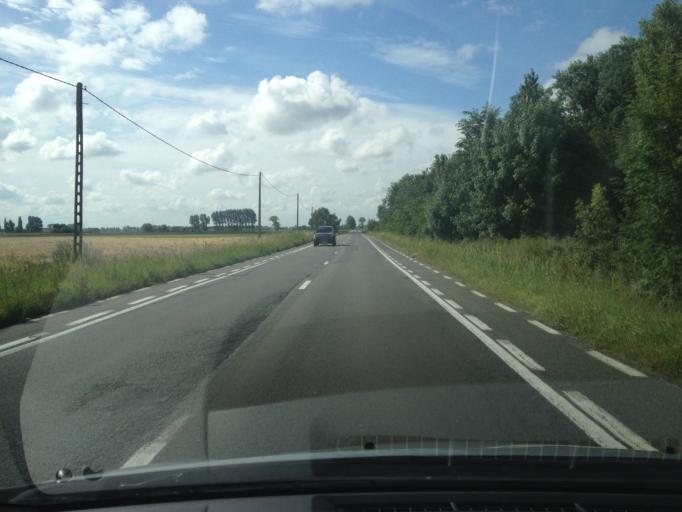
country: BE
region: Flanders
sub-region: Provincie West-Vlaanderen
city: Veurne
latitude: 51.0397
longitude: 2.6736
